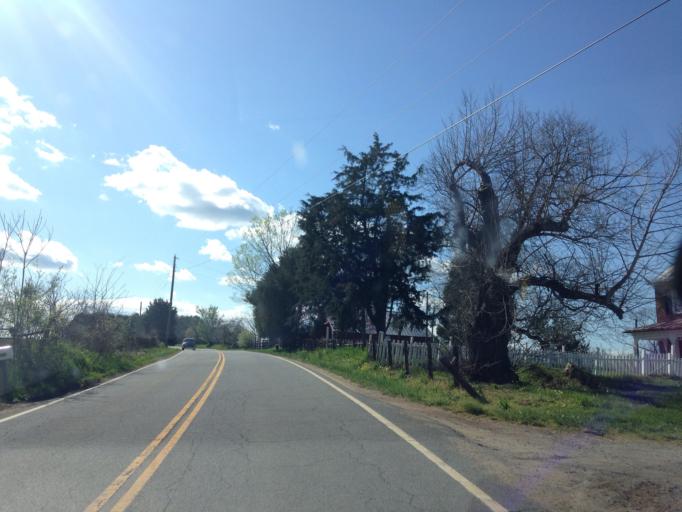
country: US
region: Maryland
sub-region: Frederick County
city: Point of Rocks
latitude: 39.2852
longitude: -77.5683
